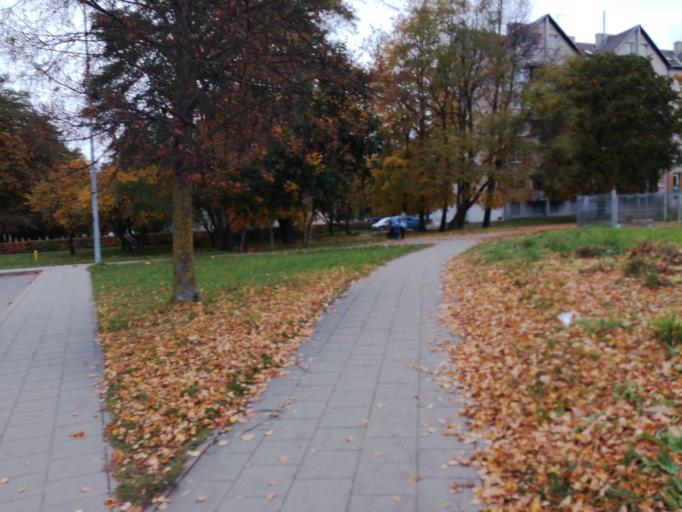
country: LT
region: Alytaus apskritis
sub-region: Alytus
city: Alytus
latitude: 54.3964
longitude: 24.0341
